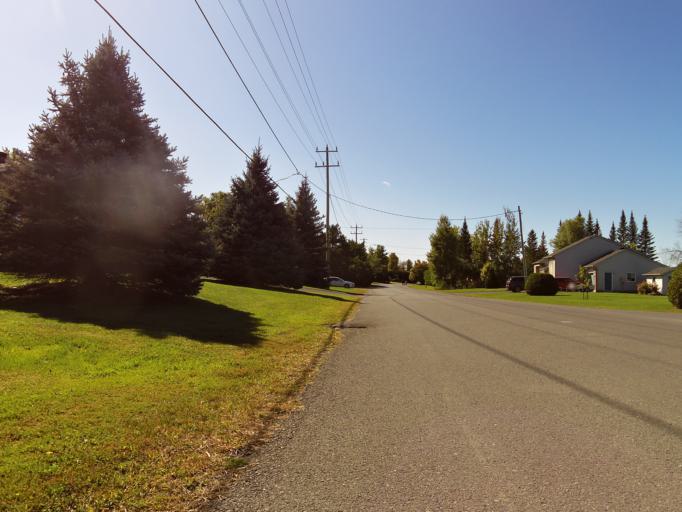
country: CA
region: Ontario
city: Casselman
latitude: 45.2681
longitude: -75.2777
